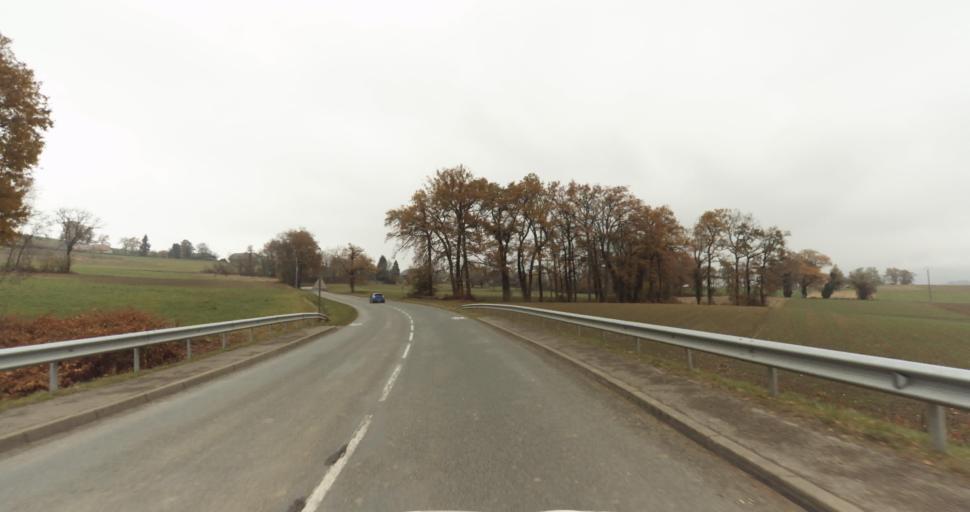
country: FR
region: Rhone-Alpes
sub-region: Departement de la Haute-Savoie
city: Alby-sur-Cheran
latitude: 45.7910
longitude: 6.0116
